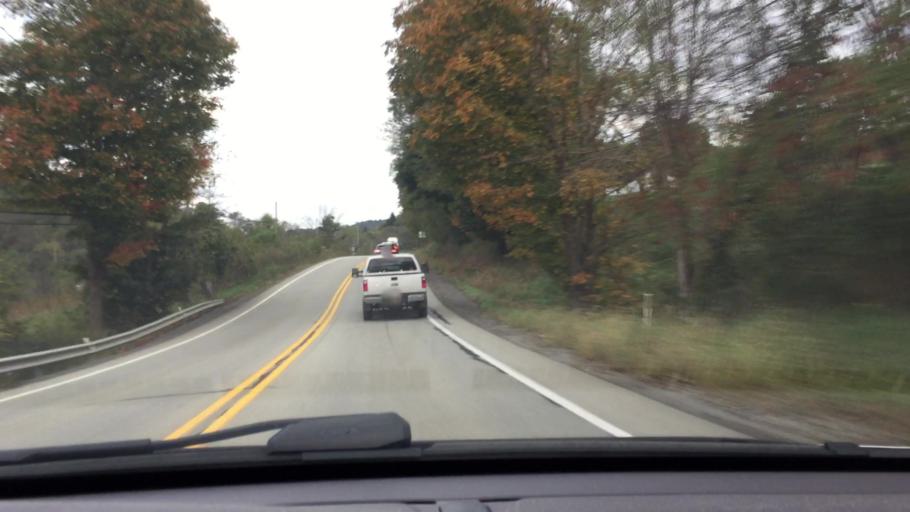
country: US
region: Pennsylvania
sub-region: Washington County
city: Canonsburg
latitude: 40.2195
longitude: -80.1536
